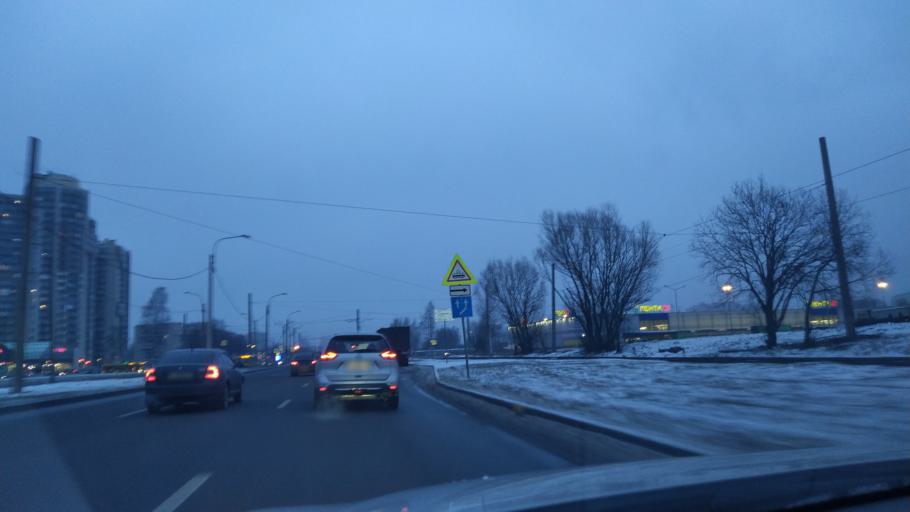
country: RU
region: Leningrad
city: Murino
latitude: 60.0291
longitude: 30.4322
